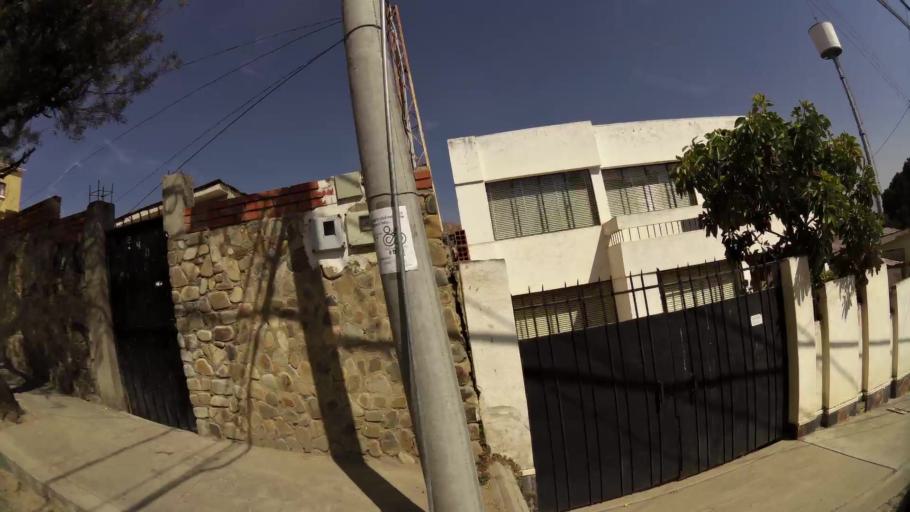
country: BO
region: La Paz
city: La Paz
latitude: -16.5413
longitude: -68.0708
